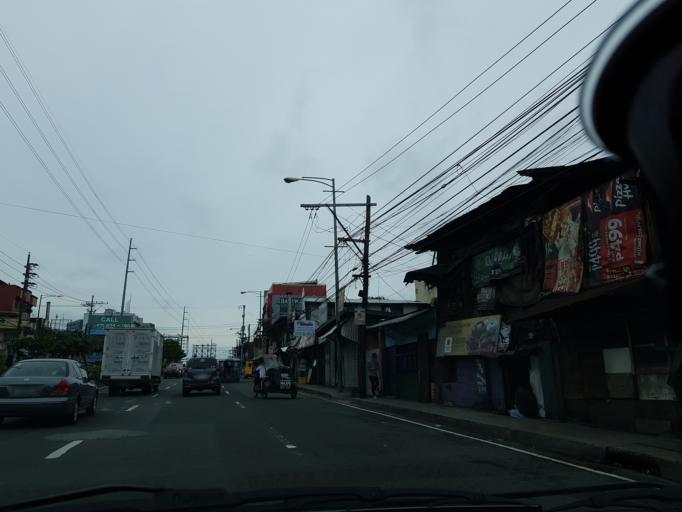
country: PH
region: Metro Manila
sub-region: Makati City
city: Makati City
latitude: 14.5597
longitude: 121.0472
